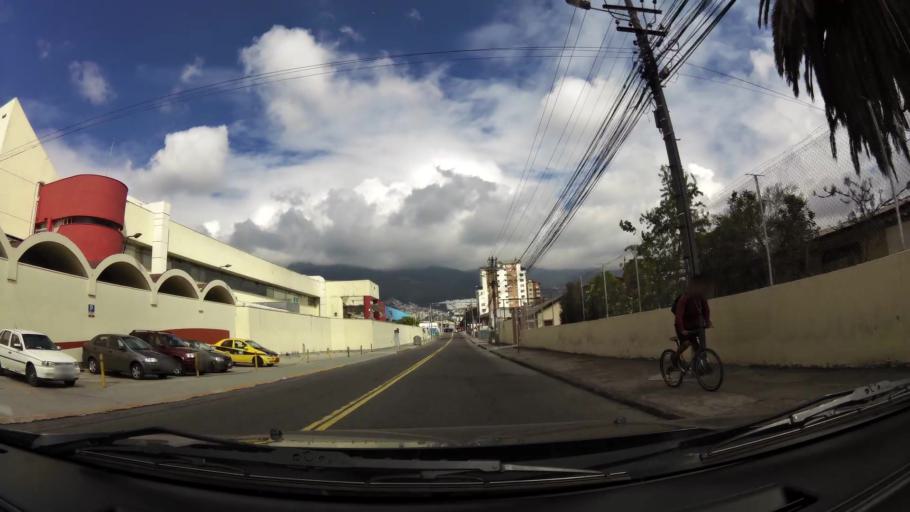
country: EC
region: Pichincha
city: Quito
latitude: -0.1533
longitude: -78.4787
